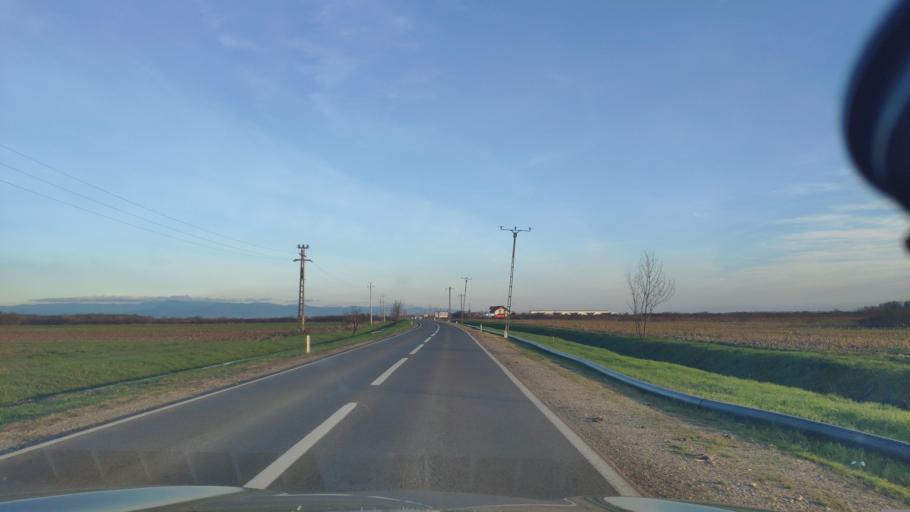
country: RO
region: Satu Mare
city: Culciu Mic
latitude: 47.7834
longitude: 23.0640
